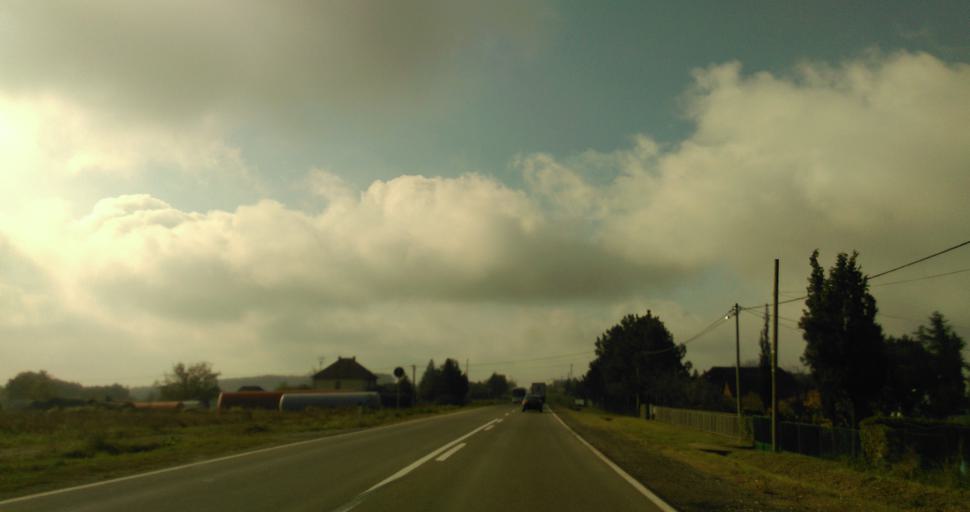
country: RS
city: Stepojevac
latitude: 44.5438
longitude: 20.3005
